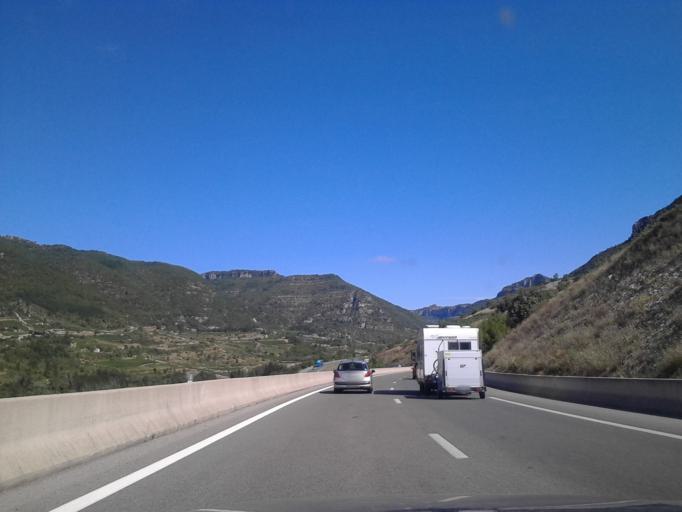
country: FR
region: Languedoc-Roussillon
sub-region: Departement de l'Herault
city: Lodeve
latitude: 43.7809
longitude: 3.3300
